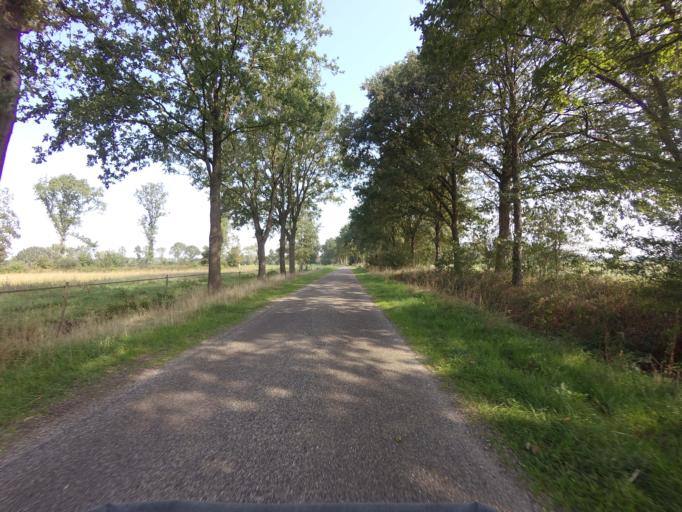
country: NL
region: Drenthe
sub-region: Gemeente Tynaarlo
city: Vries
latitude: 53.1312
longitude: 6.5275
